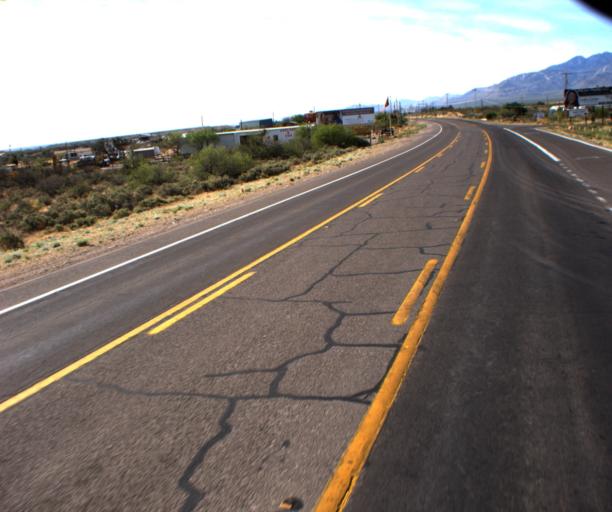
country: US
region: Arizona
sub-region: Graham County
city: Cactus Flat
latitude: 32.7797
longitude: -109.7157
